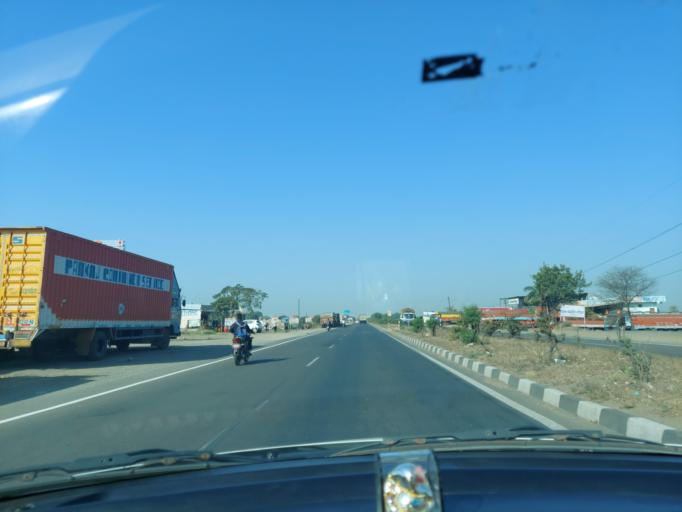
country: IN
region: Madhya Pradesh
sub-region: Indore
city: Pithampur
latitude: 22.6117
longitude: 75.7844
